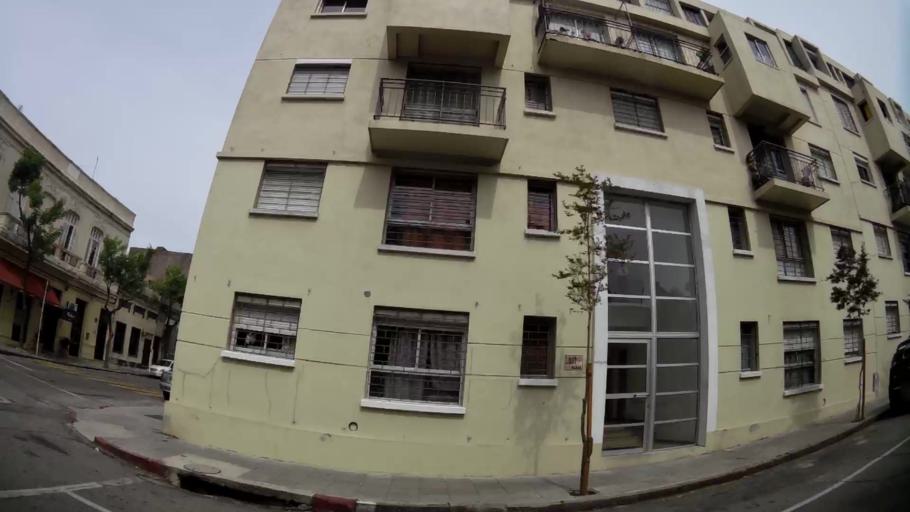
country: UY
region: Montevideo
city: Montevideo
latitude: -34.9113
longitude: -56.1792
